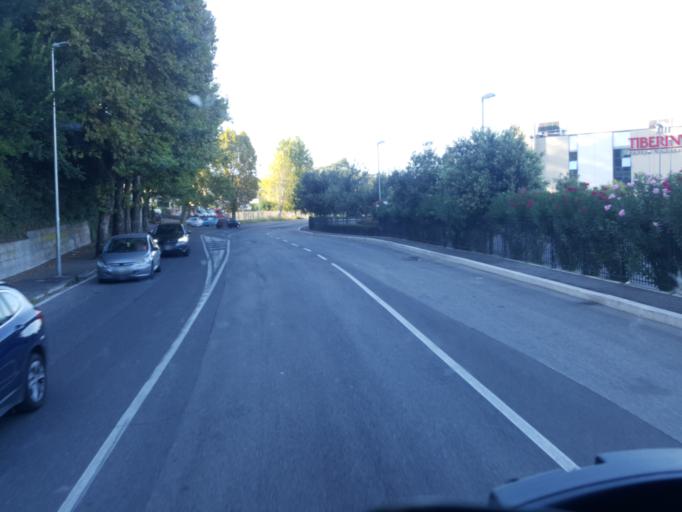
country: IT
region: Latium
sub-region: Citta metropolitana di Roma Capitale
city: Girardi-Bellavista-Terrazze
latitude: 42.1039
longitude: 12.5829
